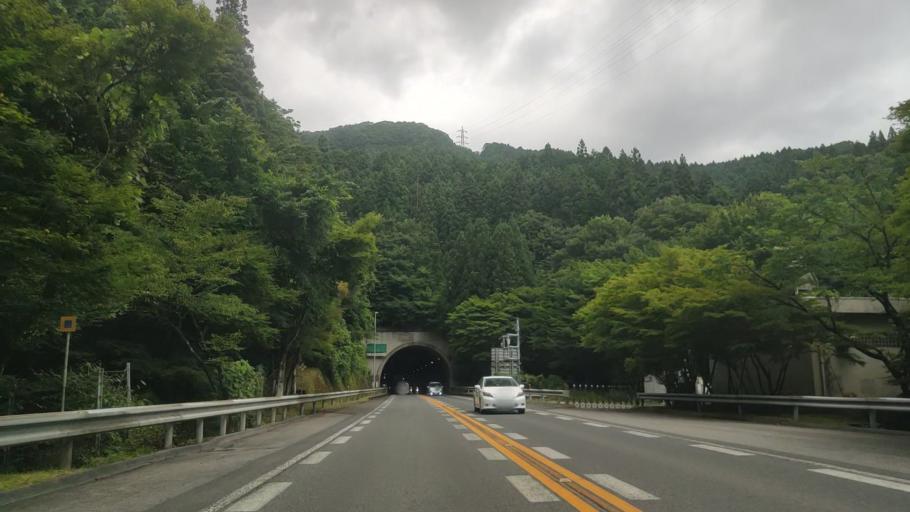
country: JP
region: Tochigi
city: Nikko
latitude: 36.7467
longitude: 139.6061
